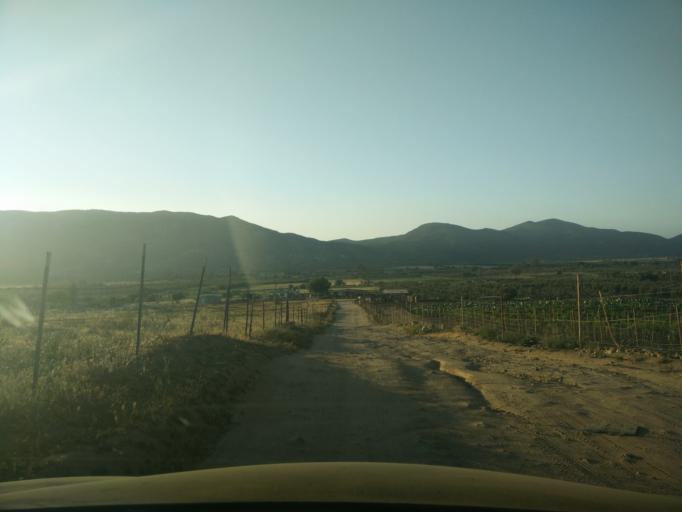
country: MX
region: Baja California
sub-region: Ensenada
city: Rancho Verde
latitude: 32.0462
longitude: -116.6450
